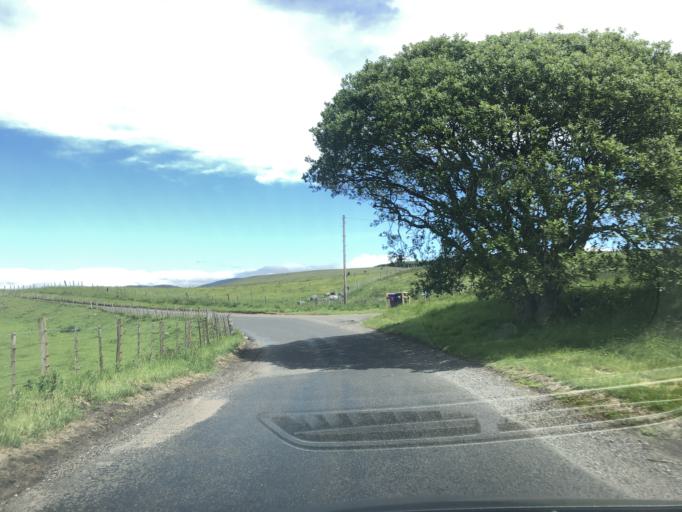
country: GB
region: Scotland
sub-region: Angus
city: Kirriemuir
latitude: 56.7562
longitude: -3.0165
